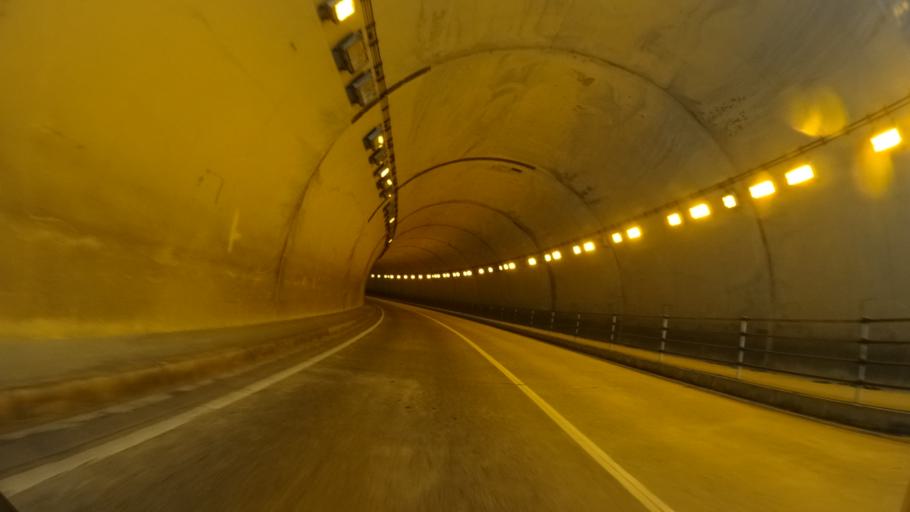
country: JP
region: Ehime
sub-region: Shikoku-chuo Shi
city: Matsuyama
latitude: 33.8698
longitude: 132.8289
